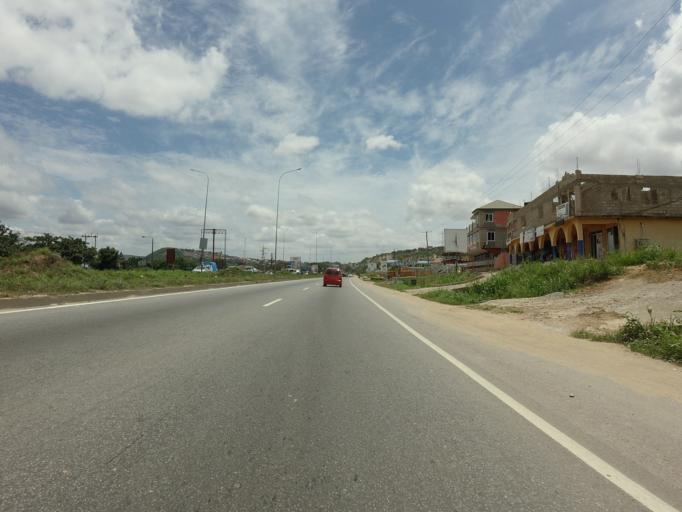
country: GH
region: Central
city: Kasoa
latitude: 5.5500
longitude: -0.3745
